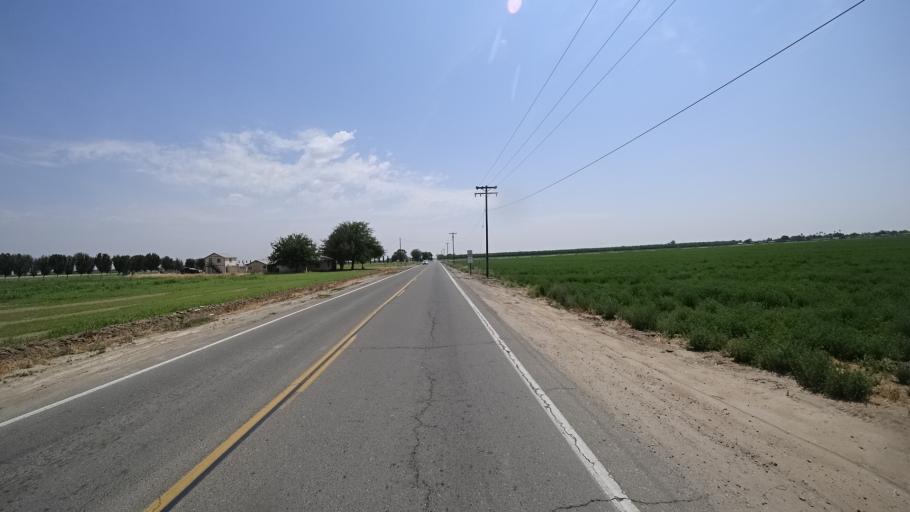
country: US
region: California
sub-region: Kings County
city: Lemoore
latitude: 36.3281
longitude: -119.7805
